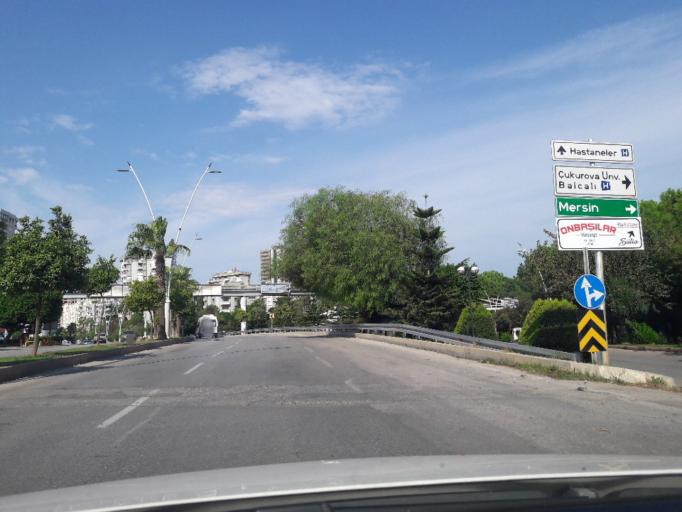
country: TR
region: Adana
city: Adana
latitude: 37.0140
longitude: 35.3275
